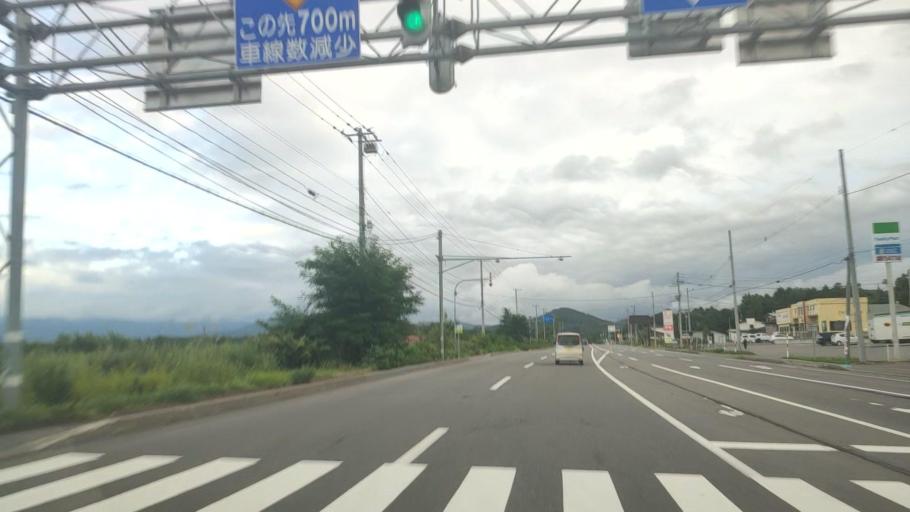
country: JP
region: Hokkaido
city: Nanae
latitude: 42.0072
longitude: 140.6318
